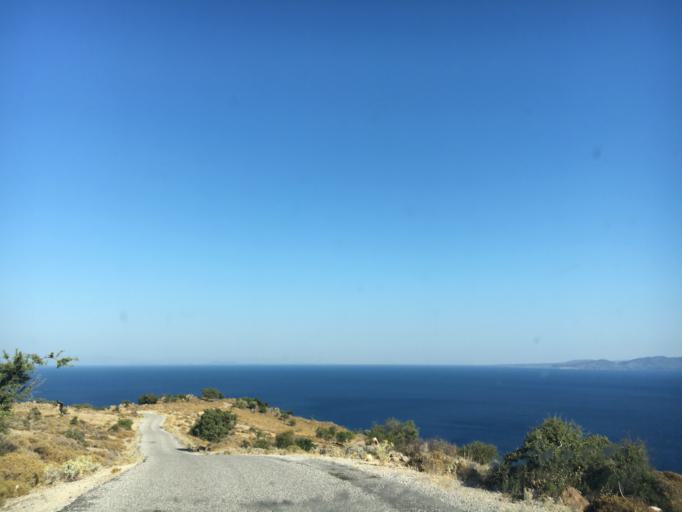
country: TR
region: Canakkale
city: Behram
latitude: 39.4880
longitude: 26.2627
